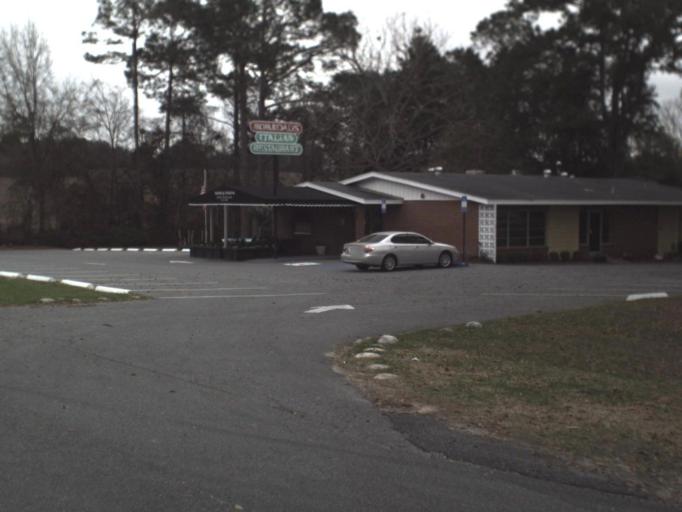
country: US
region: Florida
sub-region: Leon County
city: Tallahassee
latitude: 30.4288
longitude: -84.1937
